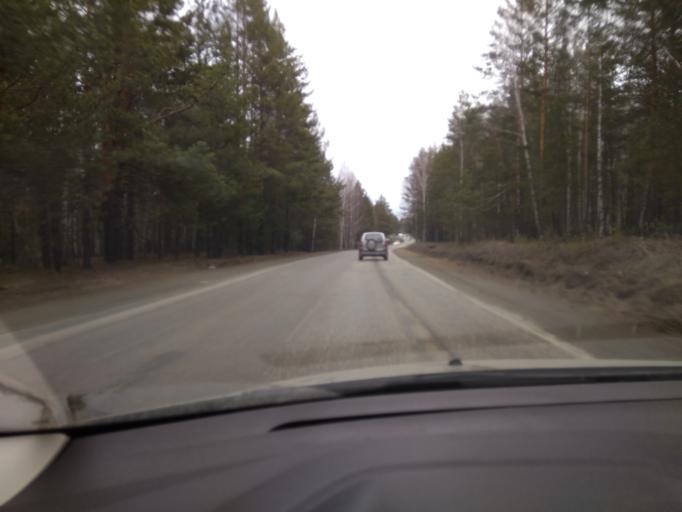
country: RU
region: Chelyabinsk
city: Kyshtym
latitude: 55.7160
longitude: 60.6199
